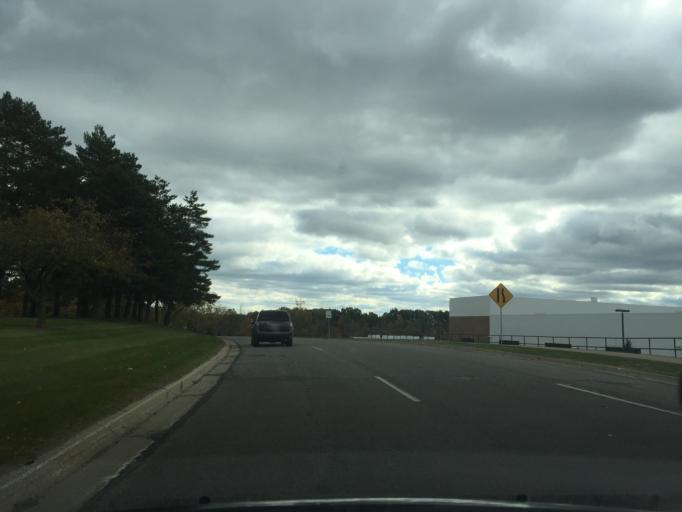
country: US
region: Michigan
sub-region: Oakland County
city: Auburn Hills
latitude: 42.6654
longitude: -83.2283
